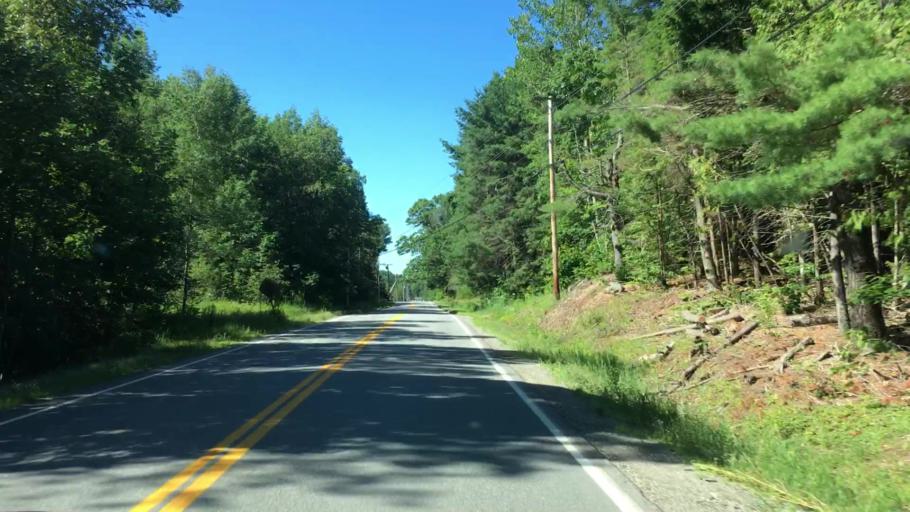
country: US
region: Maine
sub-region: Hancock County
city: Dedham
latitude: 44.7143
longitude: -68.6463
